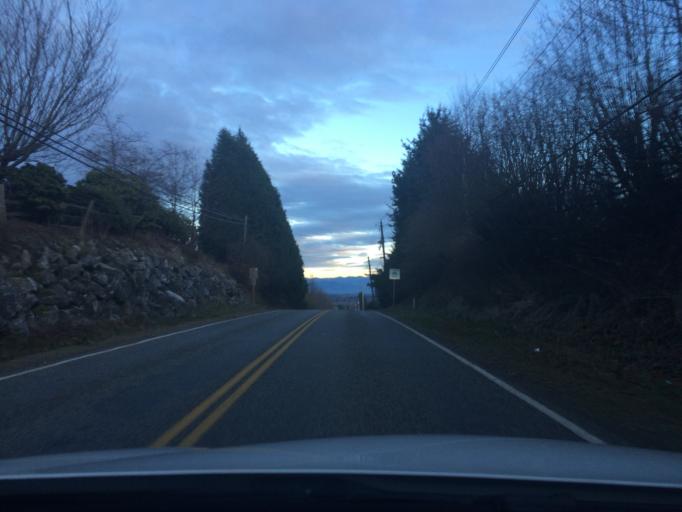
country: US
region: Washington
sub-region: Whatcom County
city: Ferndale
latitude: 48.8483
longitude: -122.6227
